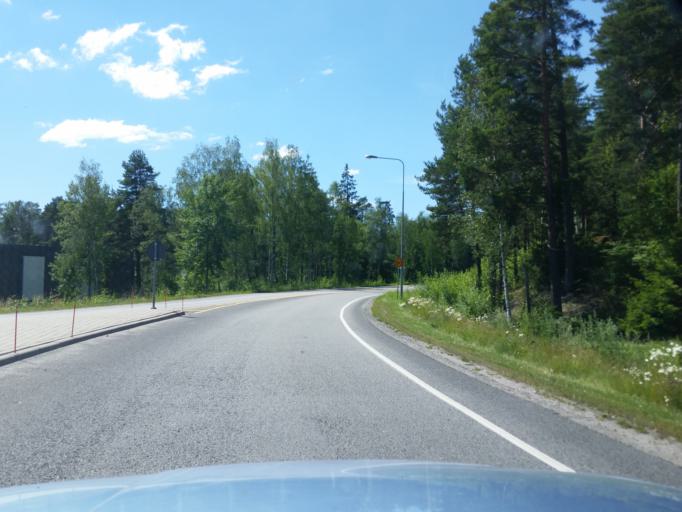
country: FI
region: Varsinais-Suomi
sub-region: Aboland-Turunmaa
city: Pargas
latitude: 60.3159
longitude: 22.3320
